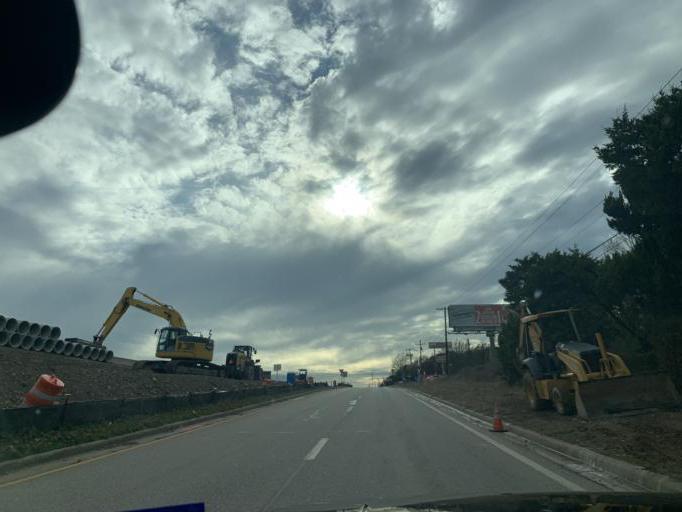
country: US
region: Texas
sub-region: Dallas County
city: Duncanville
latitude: 32.6242
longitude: -96.9102
